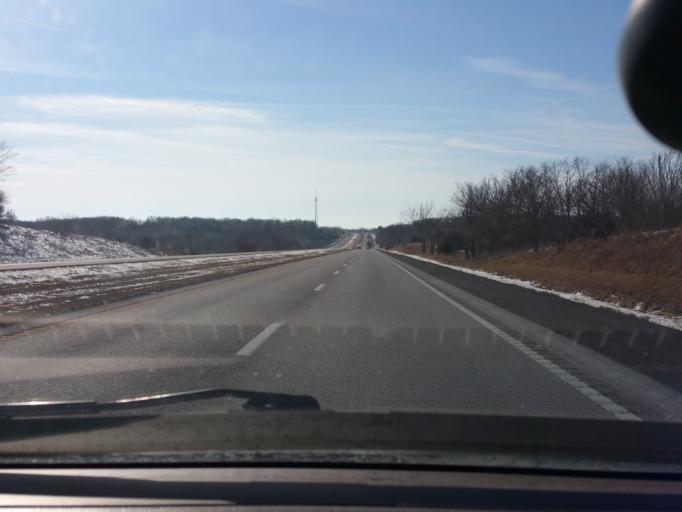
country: US
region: Missouri
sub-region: Clinton County
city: Cameron
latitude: 39.8830
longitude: -94.1614
